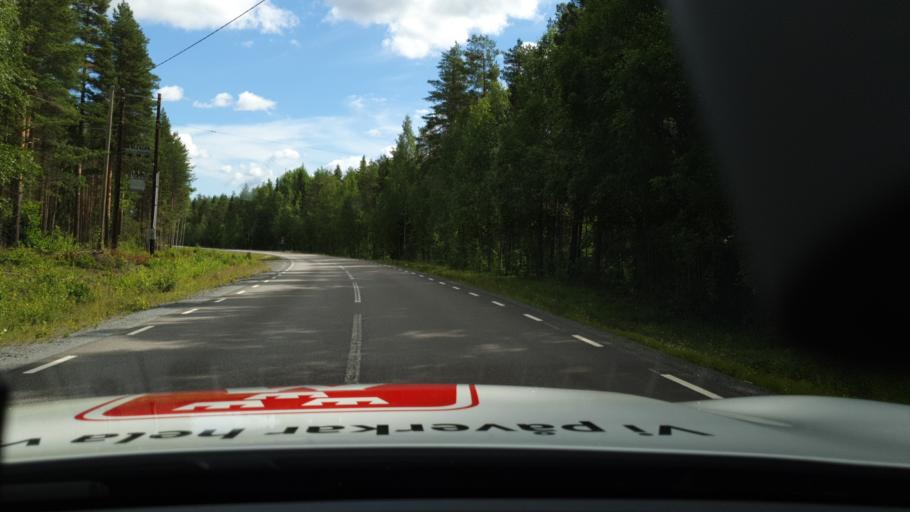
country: SE
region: Norrbotten
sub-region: Lulea Kommun
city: Sodra Sunderbyn
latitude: 65.8203
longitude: 21.8967
